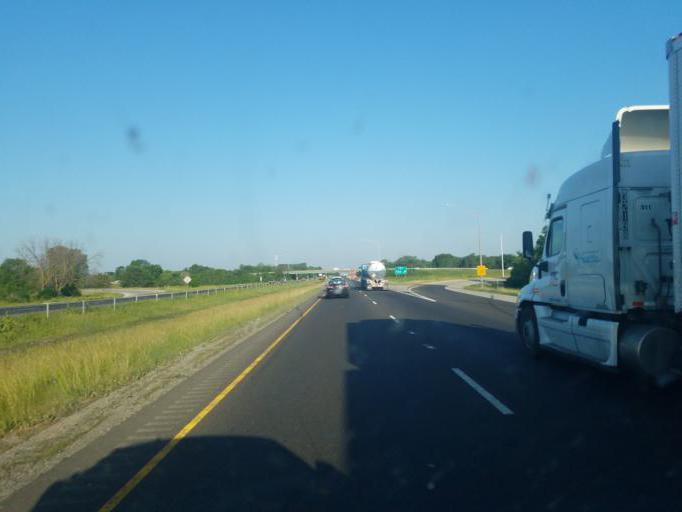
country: US
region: Illinois
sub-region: Will County
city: Ingalls Park
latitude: 41.5134
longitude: -88.0381
